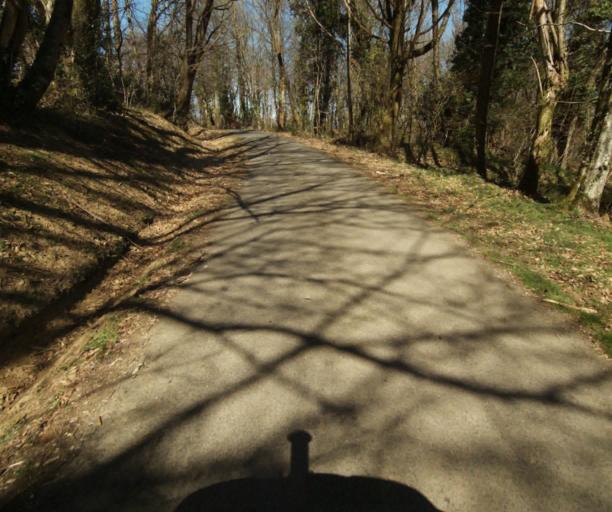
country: FR
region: Limousin
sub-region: Departement de la Correze
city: Saint-Clement
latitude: 45.3874
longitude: 1.6524
